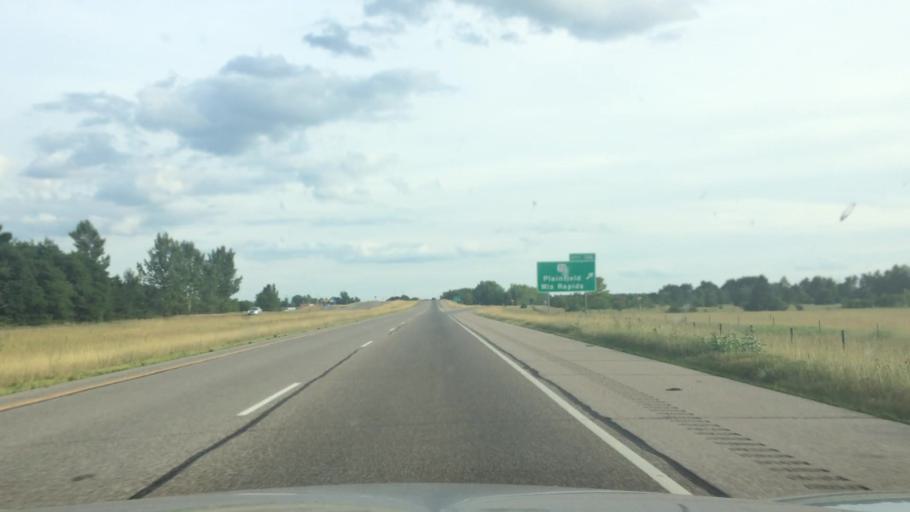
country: US
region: Wisconsin
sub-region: Portage County
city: Plover
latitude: 44.2200
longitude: -89.5248
